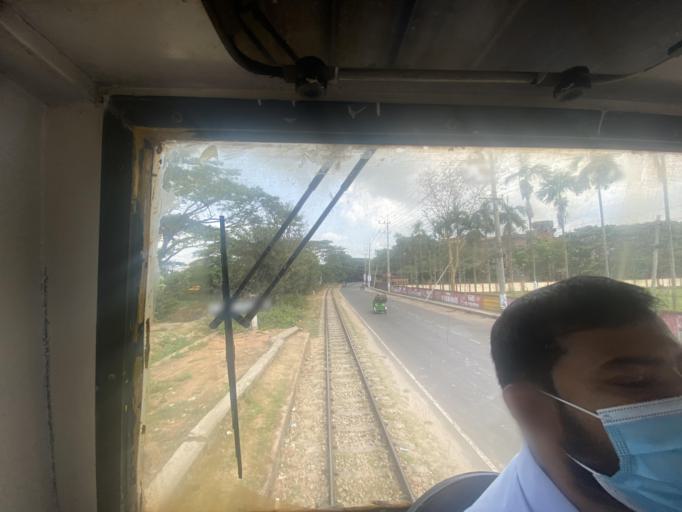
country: BD
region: Chittagong
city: Chittagong
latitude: 22.3267
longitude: 91.7768
